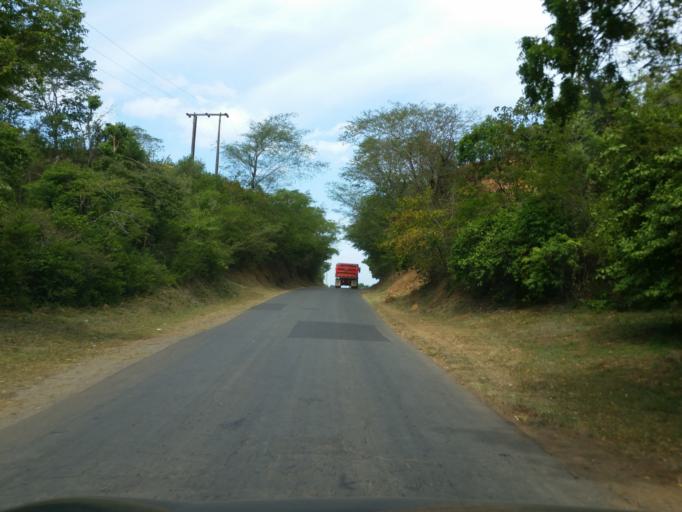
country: NI
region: Managua
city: Masachapa
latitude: 11.8148
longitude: -86.4809
